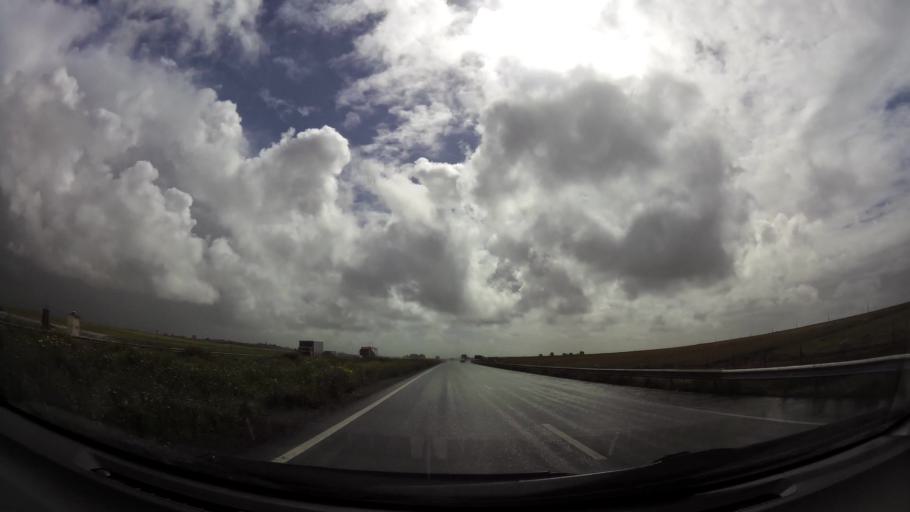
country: MA
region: Grand Casablanca
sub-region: Nouaceur
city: Dar Bouazza
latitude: 33.3805
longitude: -7.8972
